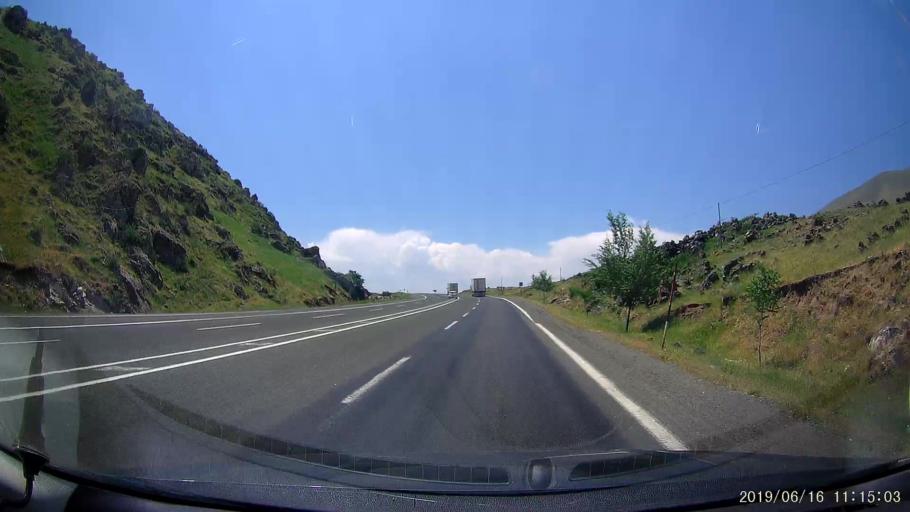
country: TR
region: Igdir
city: Igdir
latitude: 39.7701
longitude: 44.1433
